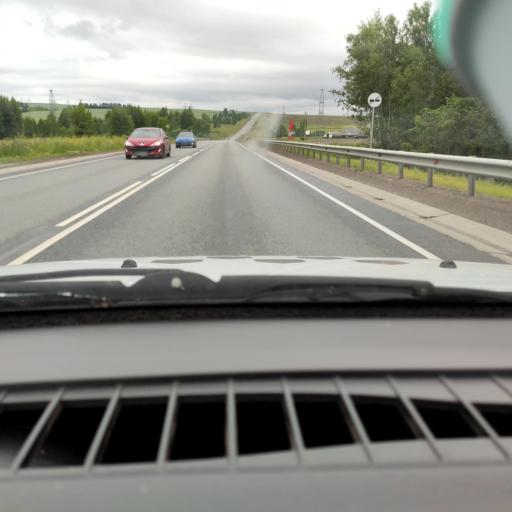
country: RU
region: Tatarstan
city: Yelabuga
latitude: 55.8192
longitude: 52.1623
